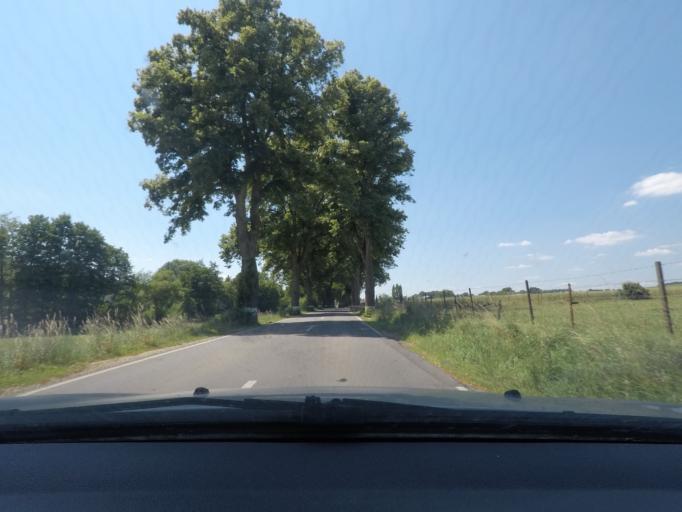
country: LU
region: Diekirch
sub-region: Canton de Redange
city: Ell
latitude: 49.7660
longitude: 5.8702
